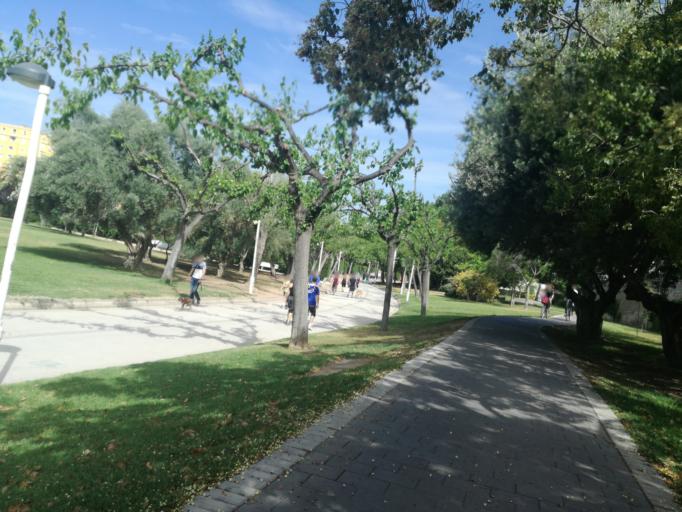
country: ES
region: Valencia
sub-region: Provincia de Valencia
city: Valencia
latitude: 39.4617
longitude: -0.3578
